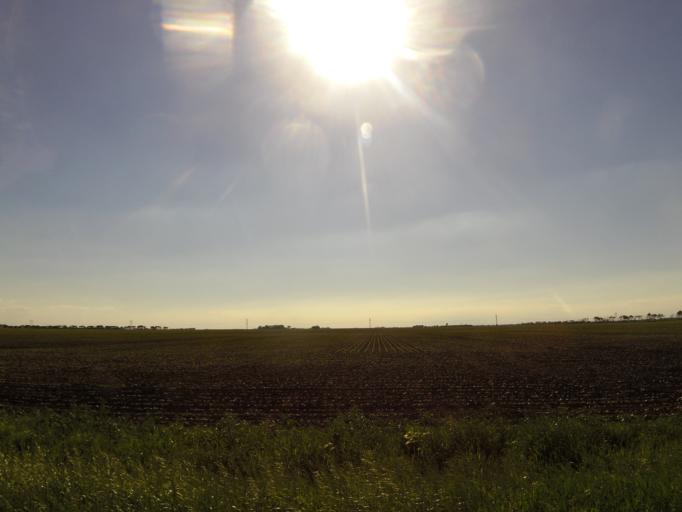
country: US
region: North Dakota
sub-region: Walsh County
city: Grafton
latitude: 48.4020
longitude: -97.2556
